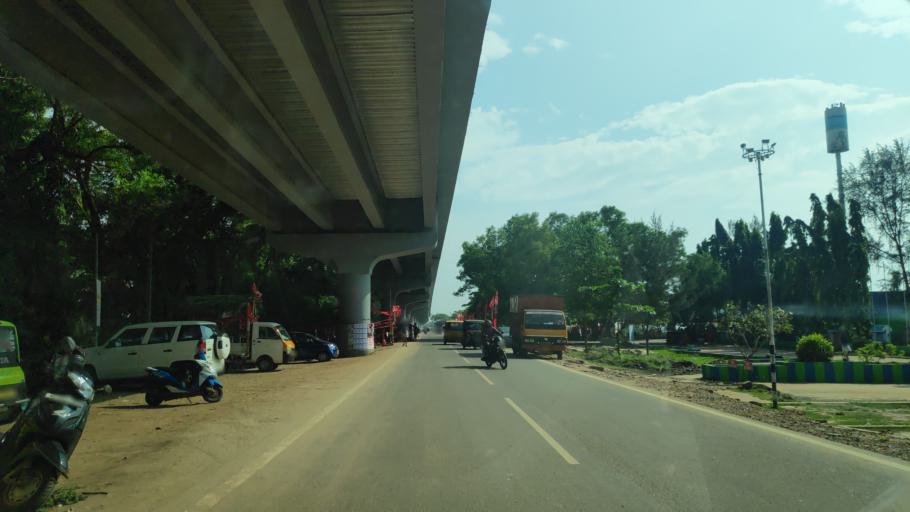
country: IN
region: Kerala
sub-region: Alappuzha
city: Alleppey
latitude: 9.4967
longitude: 76.3179
